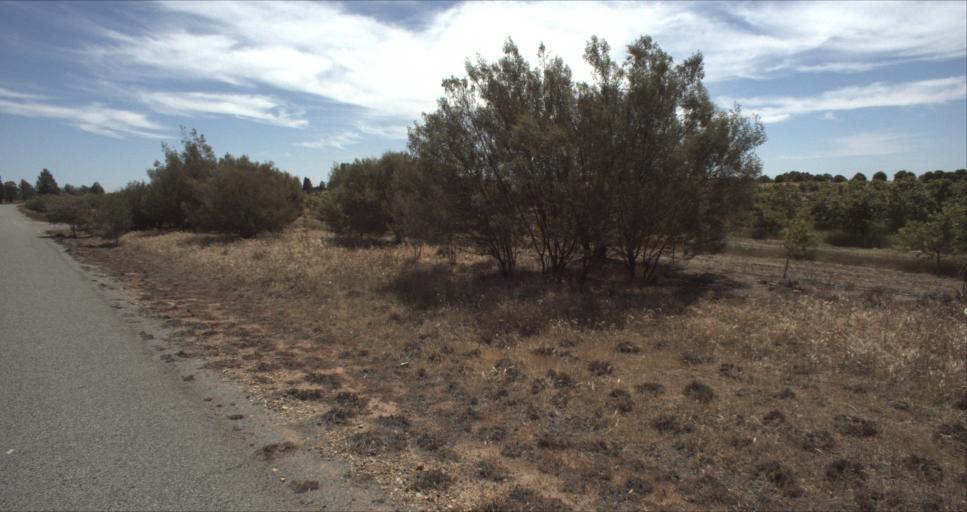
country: AU
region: New South Wales
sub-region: Leeton
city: Leeton
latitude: -34.6701
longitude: 146.4492
